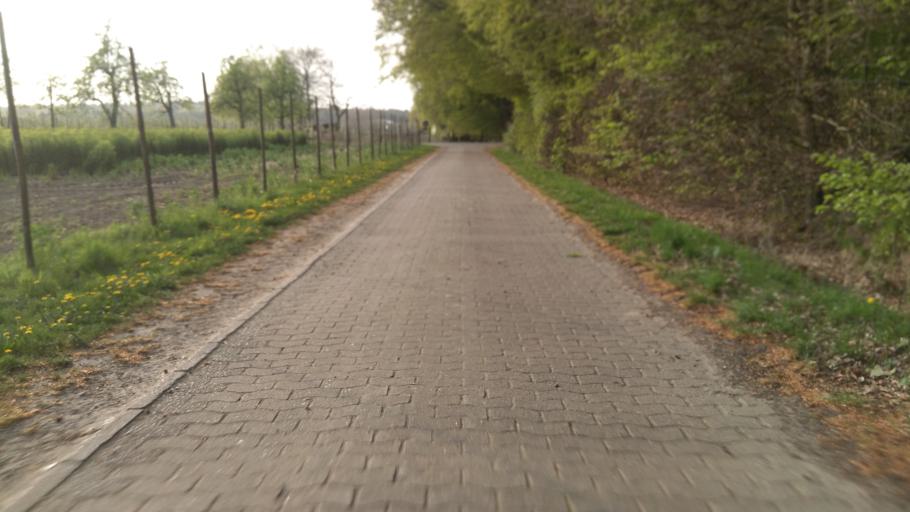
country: DE
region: Lower Saxony
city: Nottensdorf
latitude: 53.4693
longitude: 9.6340
